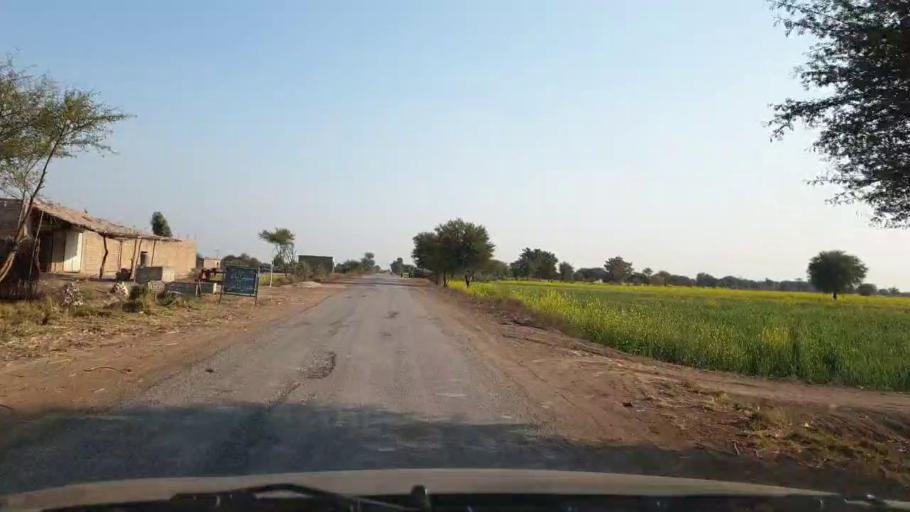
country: PK
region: Sindh
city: Jhol
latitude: 25.9521
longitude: 68.9008
